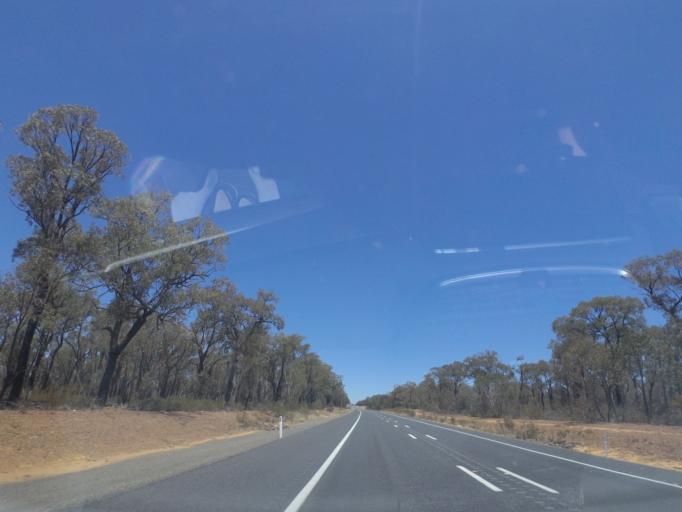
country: AU
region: New South Wales
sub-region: Warrumbungle Shire
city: Coonabarabran
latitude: -30.8890
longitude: 149.4431
